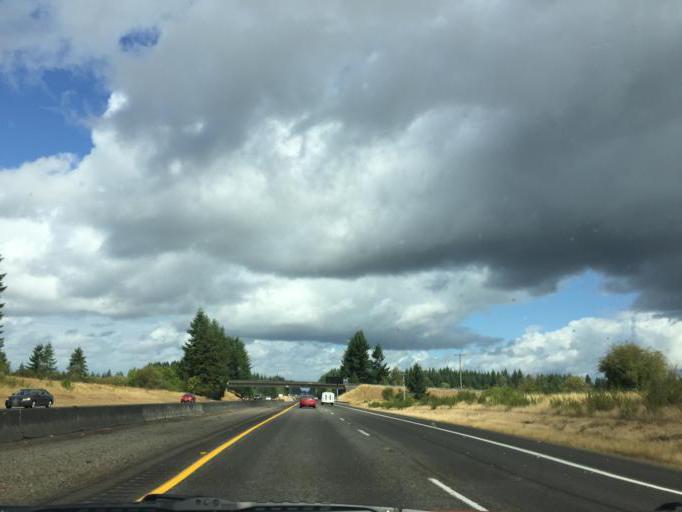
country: US
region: Washington
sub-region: Lewis County
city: Winlock
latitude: 46.5154
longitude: -122.8765
